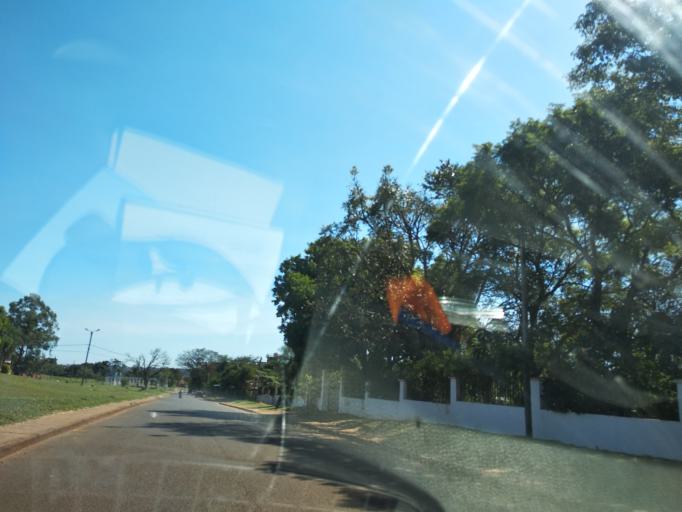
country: AR
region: Misiones
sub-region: Departamento de Capital
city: Posadas
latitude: -27.4251
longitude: -55.8818
